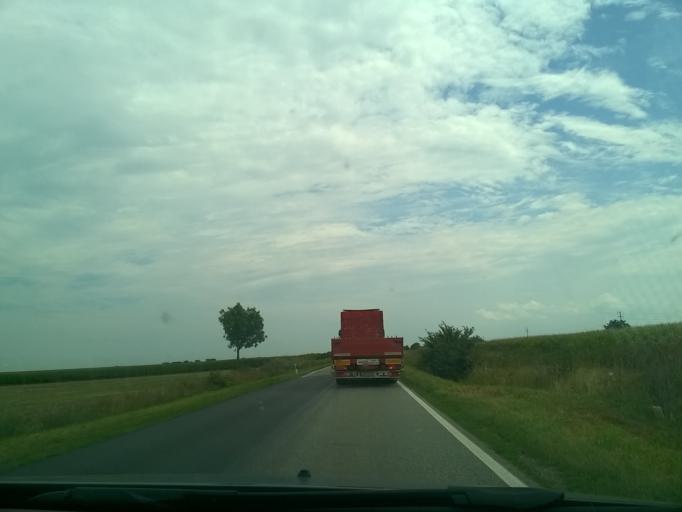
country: RS
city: Klek
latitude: 45.3844
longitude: 20.4561
